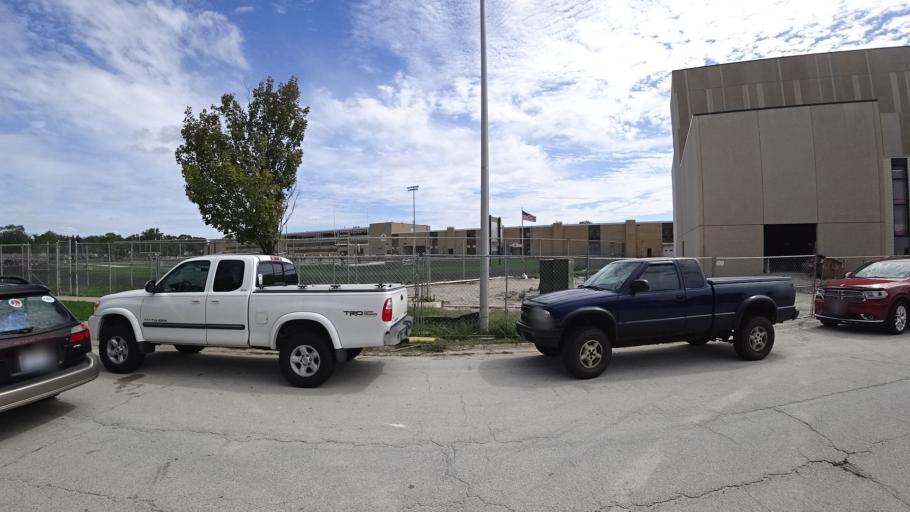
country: US
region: Illinois
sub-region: Cook County
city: Burbank
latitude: 41.7215
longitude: -87.7702
